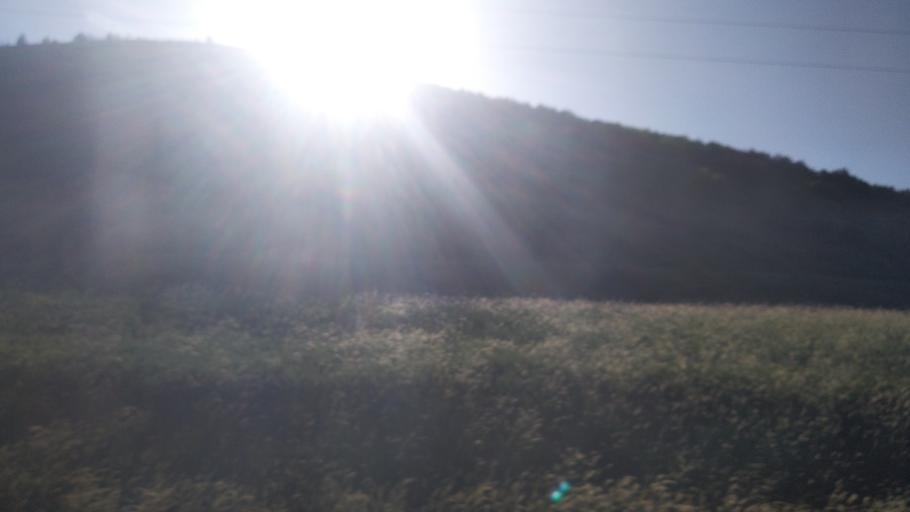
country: TR
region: Bitlis
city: Resadiye
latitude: 38.4668
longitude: 42.5441
